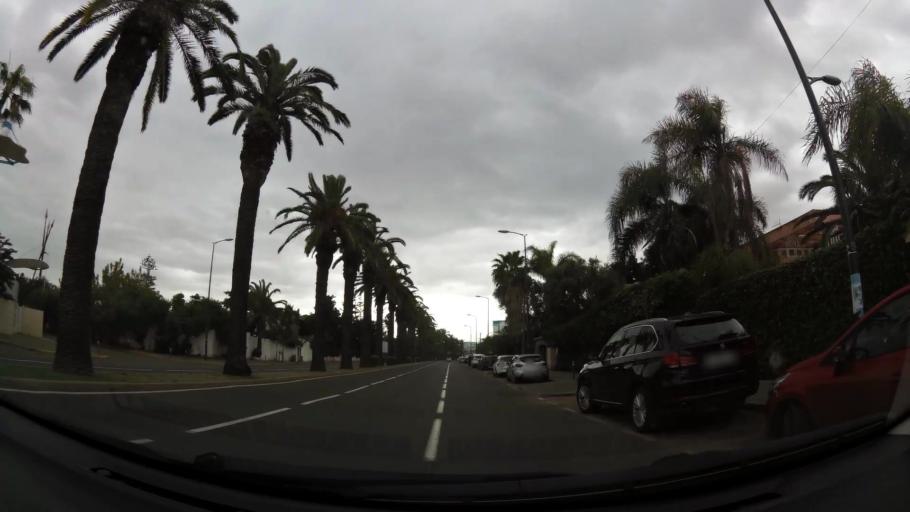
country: MA
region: Grand Casablanca
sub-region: Casablanca
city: Casablanca
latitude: 33.5808
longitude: -7.6583
